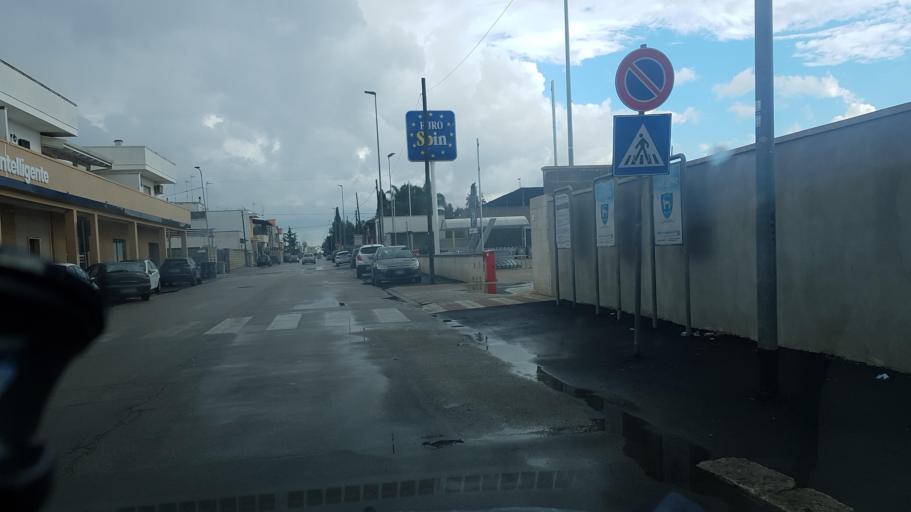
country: IT
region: Apulia
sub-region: Provincia di Lecce
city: Carmiano
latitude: 40.3381
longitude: 18.0425
